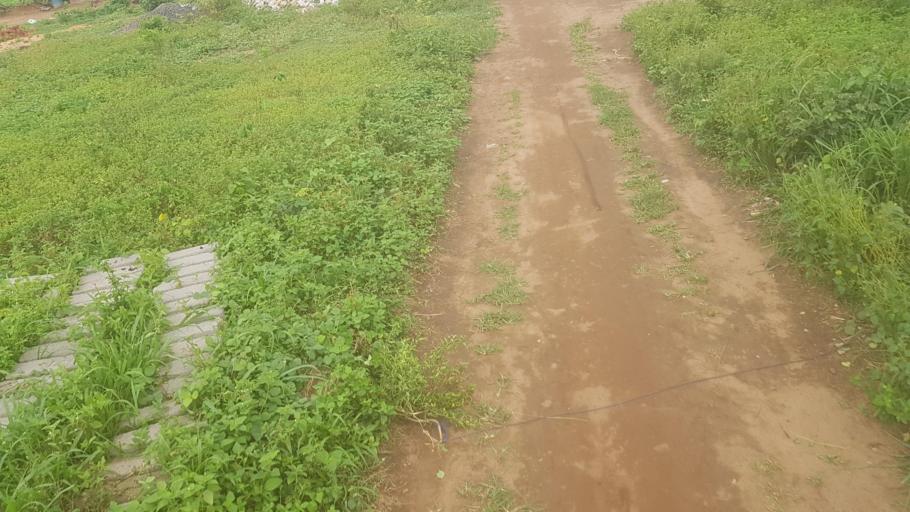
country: SL
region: Southern Province
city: Mogbwemo
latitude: 7.6141
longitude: -12.1752
